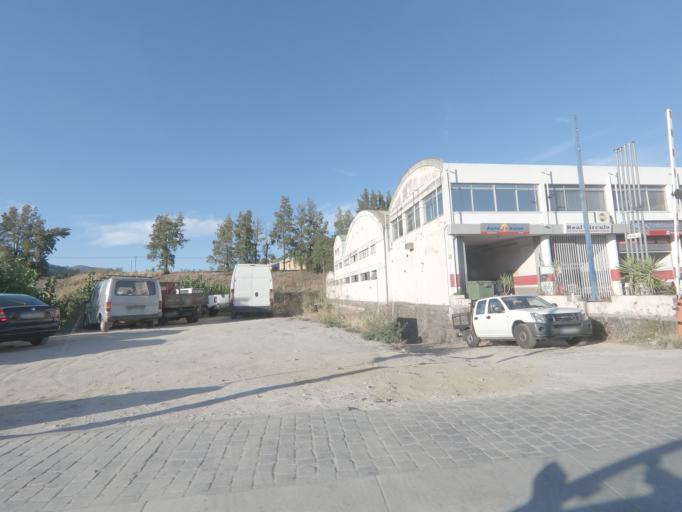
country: PT
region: Vila Real
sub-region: Peso da Regua
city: Peso da Regua
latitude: 41.1648
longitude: -7.7944
